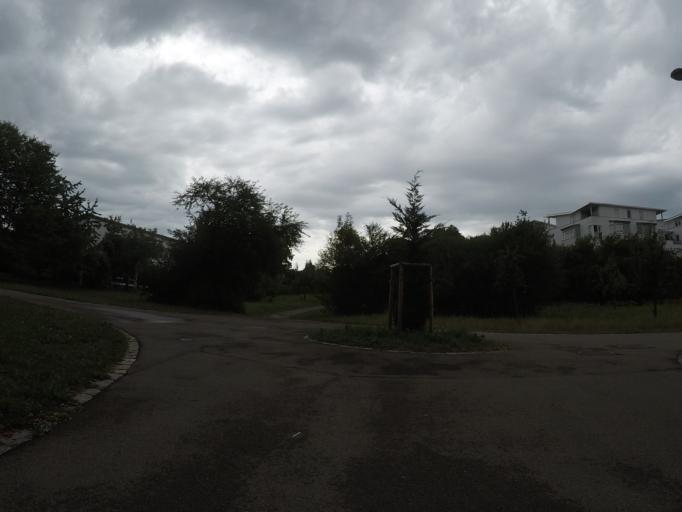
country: DE
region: Baden-Wuerttemberg
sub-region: Tuebingen Region
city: Reutlingen
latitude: 48.4857
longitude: 9.1892
